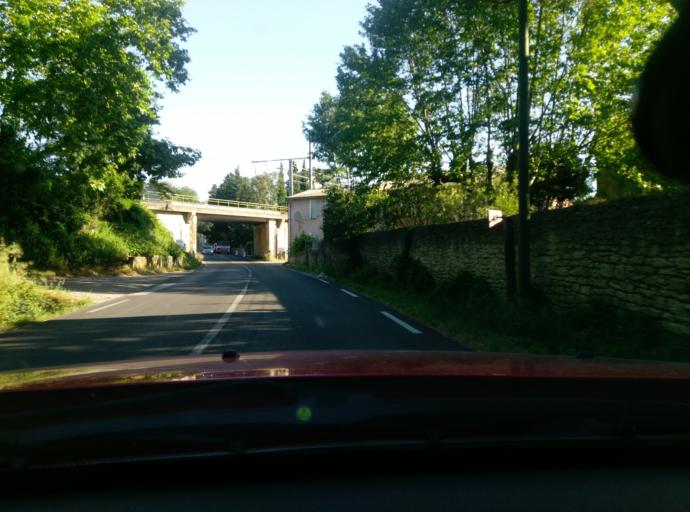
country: FR
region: Languedoc-Roussillon
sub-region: Departement du Gard
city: Remoulins
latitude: 43.9321
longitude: 4.5598
